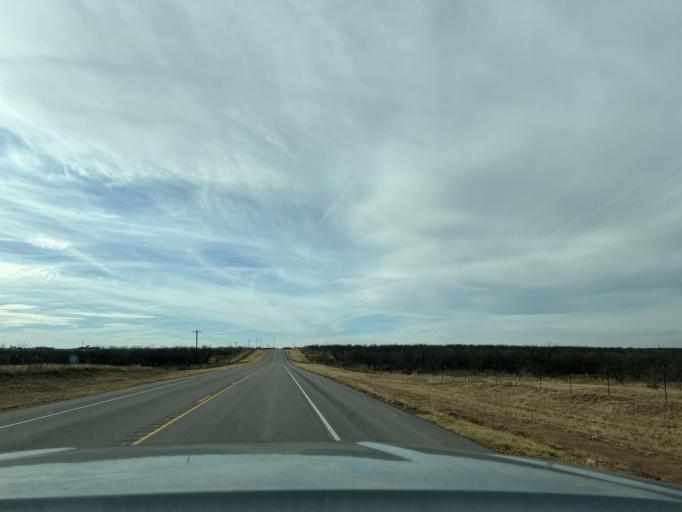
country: US
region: Texas
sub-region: Jones County
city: Anson
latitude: 32.7506
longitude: -99.6937
